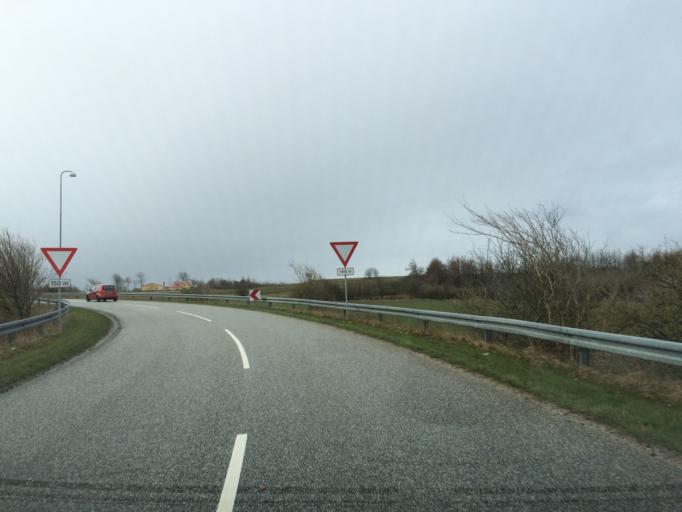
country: DK
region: Central Jutland
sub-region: Ringkobing-Skjern Kommune
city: Videbaek
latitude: 56.1939
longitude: 8.5677
